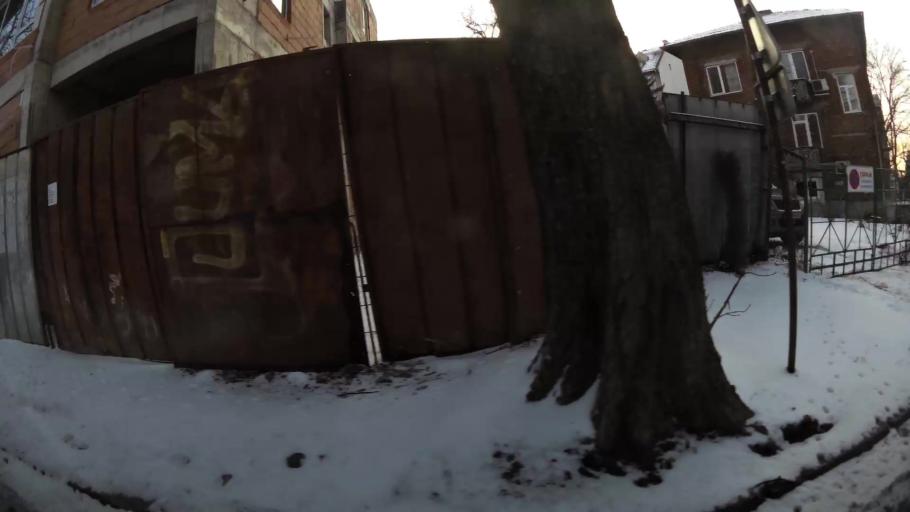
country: BG
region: Sofia-Capital
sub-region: Stolichna Obshtina
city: Sofia
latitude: 42.6952
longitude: 23.3629
